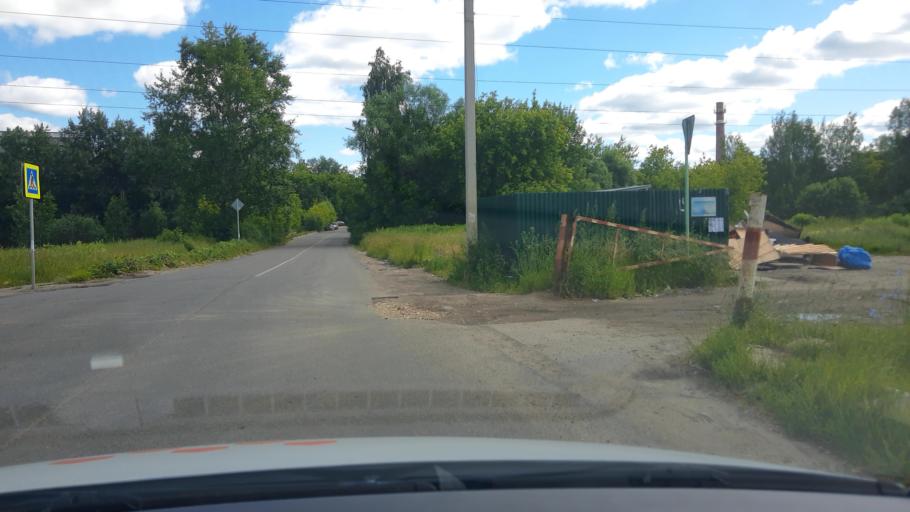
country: RU
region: Moskovskaya
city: Noginsk
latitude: 55.8760
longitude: 38.4418
